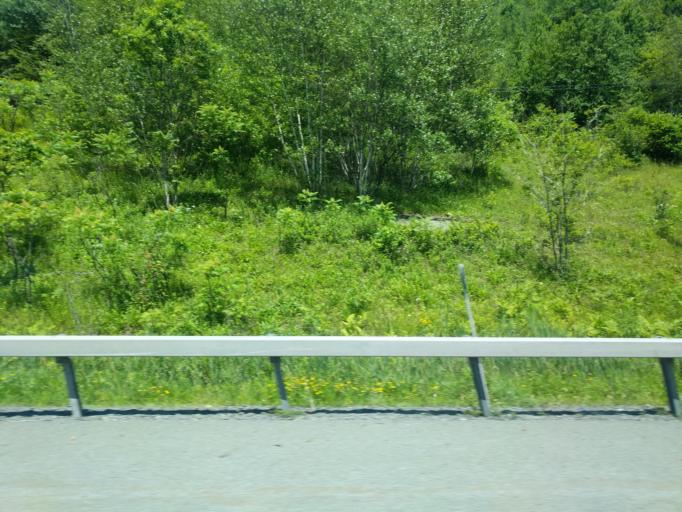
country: US
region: New York
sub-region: Sullivan County
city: Livingston Manor
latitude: 41.8734
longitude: -74.7958
